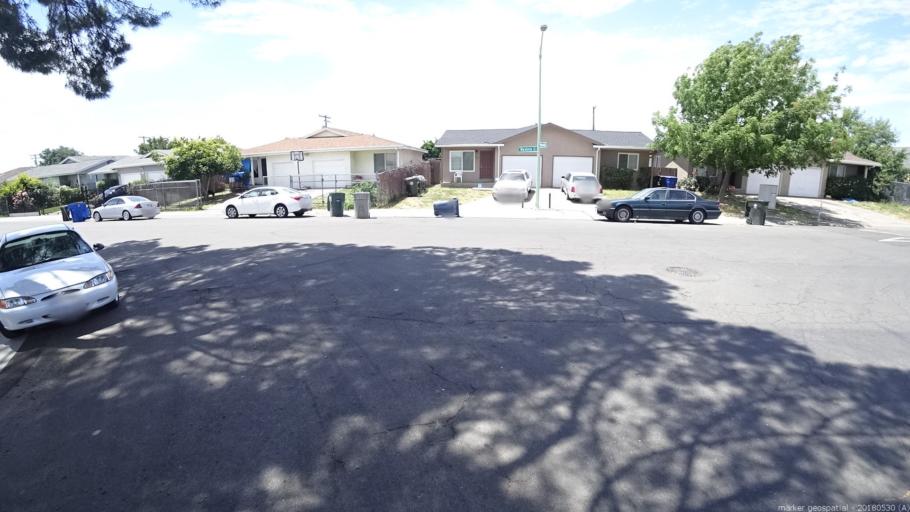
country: US
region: California
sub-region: Sacramento County
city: Sacramento
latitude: 38.6253
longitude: -121.4677
